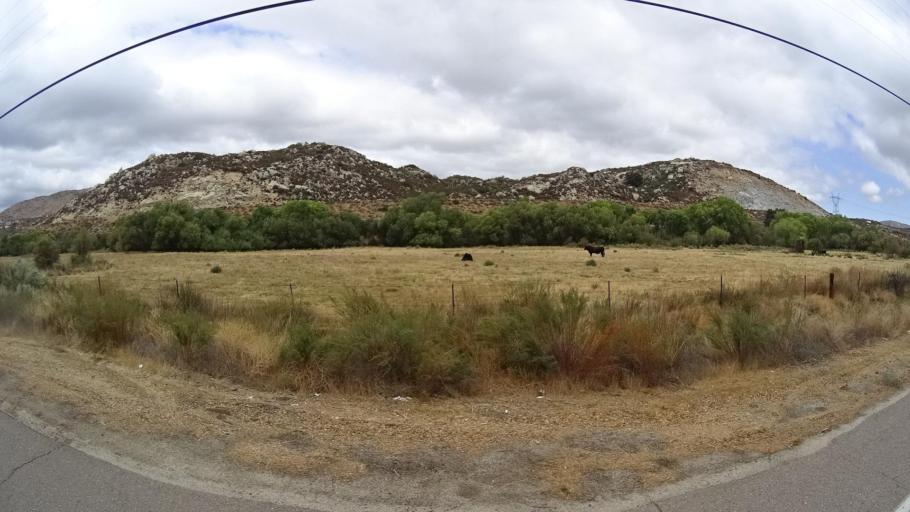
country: US
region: California
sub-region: San Diego County
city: Campo
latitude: 32.7233
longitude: -116.4383
